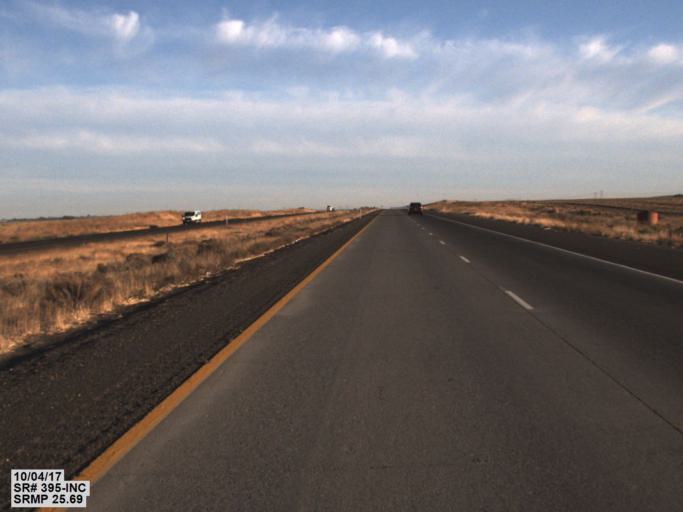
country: US
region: Washington
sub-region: Franklin County
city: Pasco
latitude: 46.2936
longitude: -119.0934
